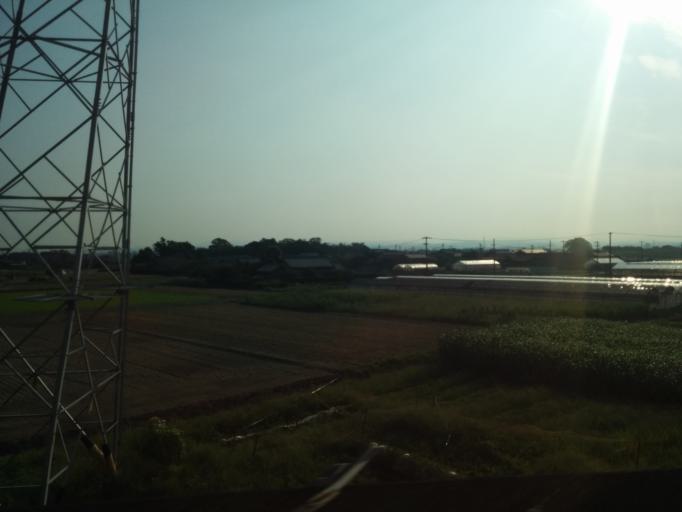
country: JP
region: Aichi
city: Anjo
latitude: 34.9229
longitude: 137.1029
